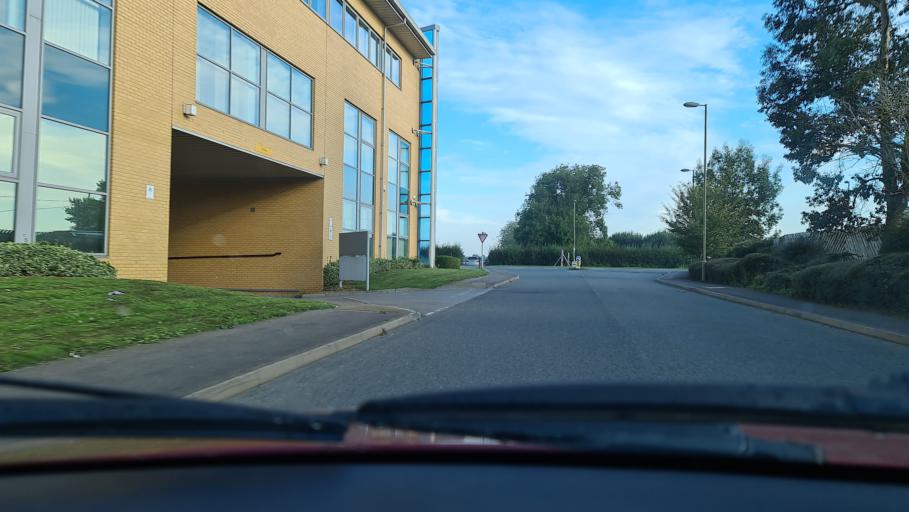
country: GB
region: England
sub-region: Oxfordshire
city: Kidlington
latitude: 51.8306
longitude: -1.3044
